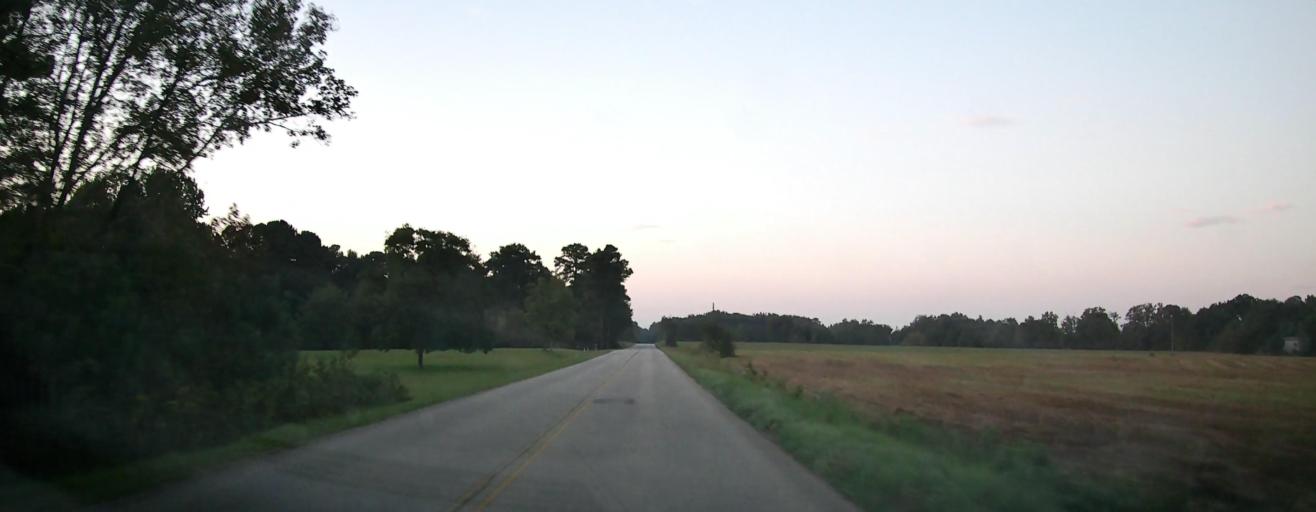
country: US
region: Georgia
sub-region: Butts County
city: Jackson
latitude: 33.3023
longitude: -84.0431
